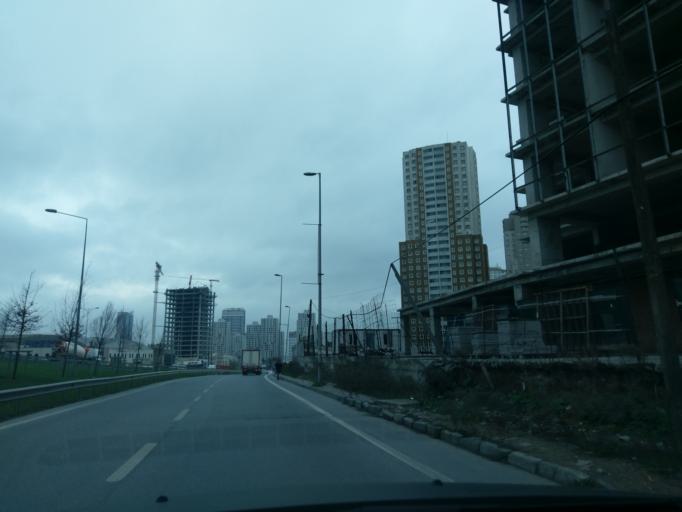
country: TR
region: Istanbul
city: Esenyurt
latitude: 41.0173
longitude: 28.6786
